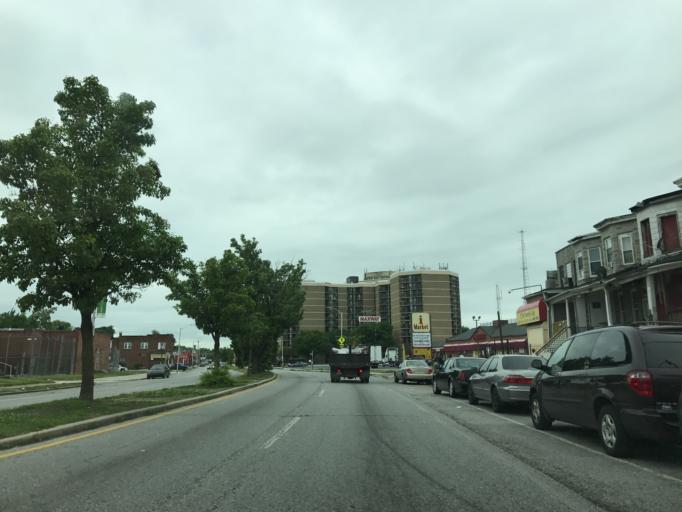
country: US
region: Maryland
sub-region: Baltimore County
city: Lochearn
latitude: 39.3463
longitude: -76.6802
